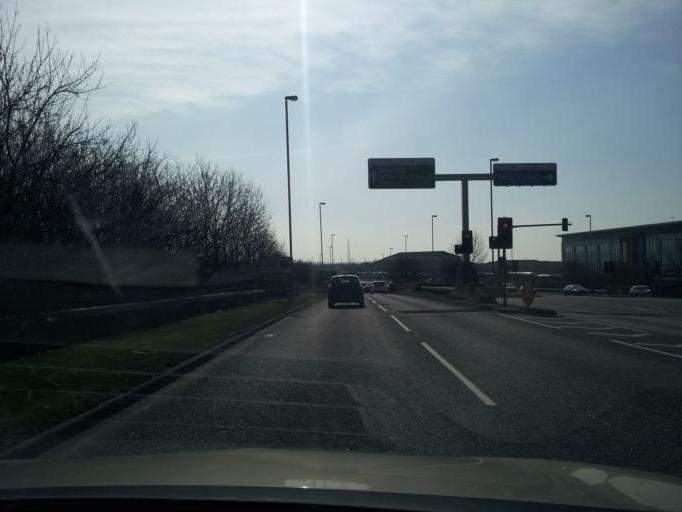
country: GB
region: England
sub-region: Leicestershire
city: Enderby
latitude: 52.5996
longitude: -1.1864
